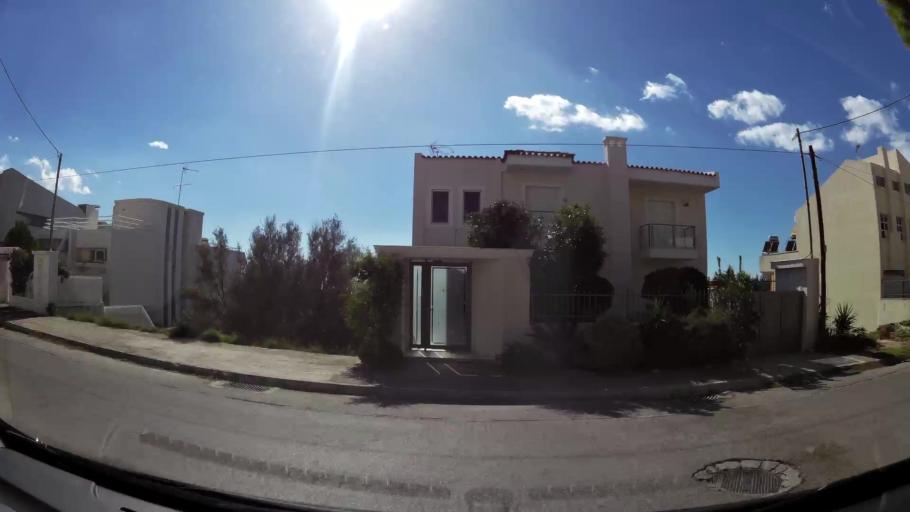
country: GR
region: Attica
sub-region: Nomarchia Anatolikis Attikis
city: Voula
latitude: 37.8483
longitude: 23.7817
